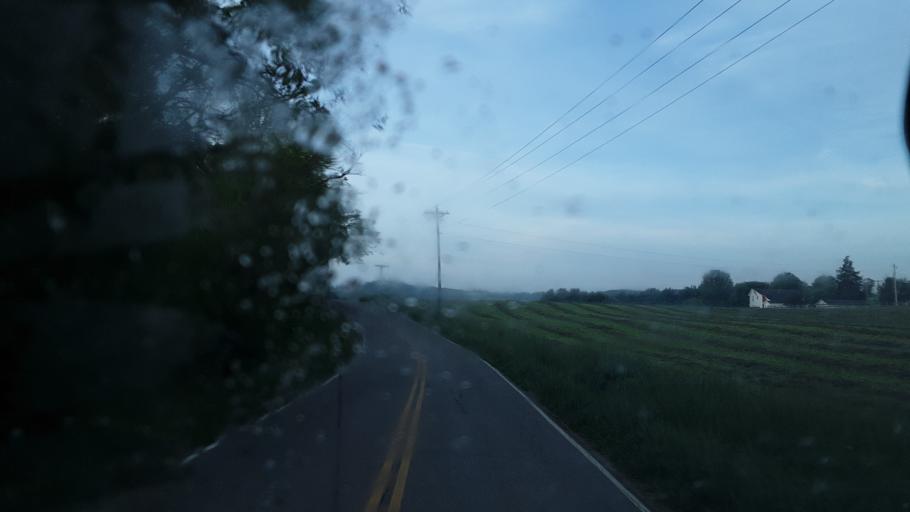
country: US
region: Ohio
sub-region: Ross County
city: Kingston
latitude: 39.5069
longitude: -82.6994
